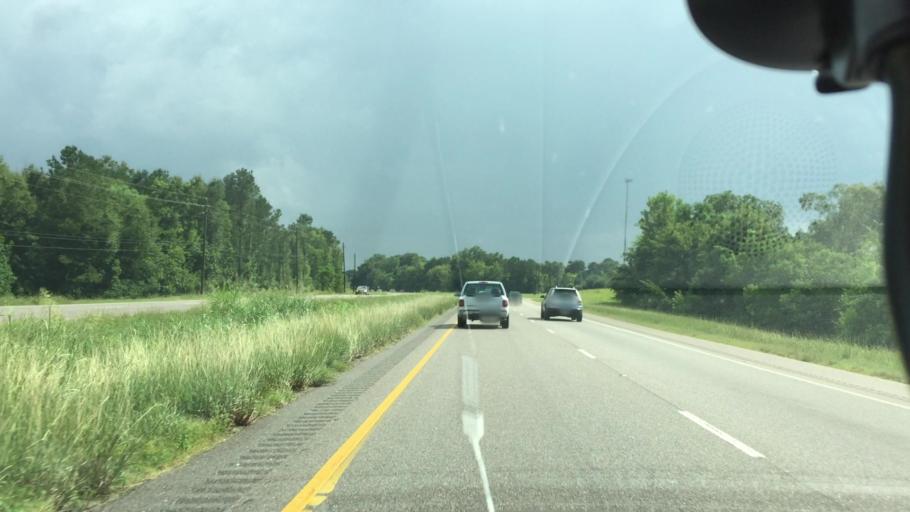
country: US
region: Alabama
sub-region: Montgomery County
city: Pike Road
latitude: 32.3048
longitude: -86.1940
